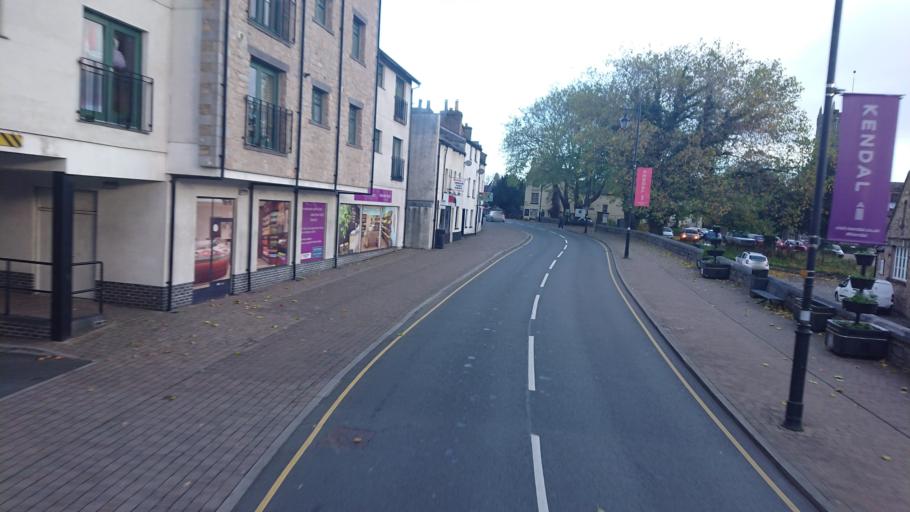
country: GB
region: England
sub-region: Cumbria
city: Kendal
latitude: 54.3215
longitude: -2.7453
